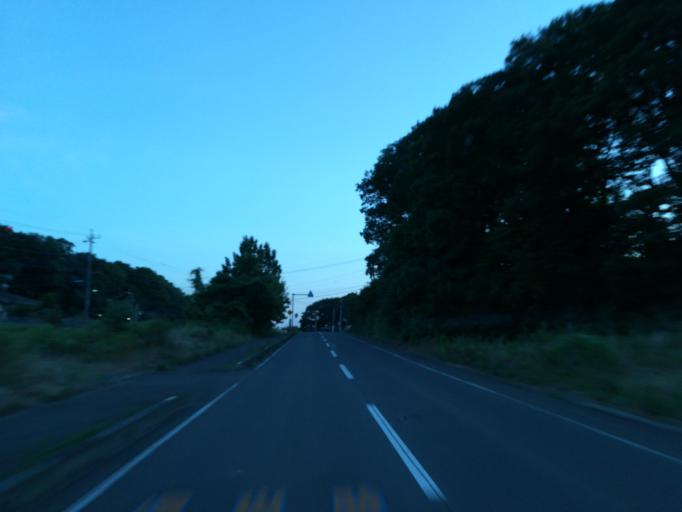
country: JP
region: Ibaraki
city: Makabe
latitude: 36.2583
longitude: 140.0592
